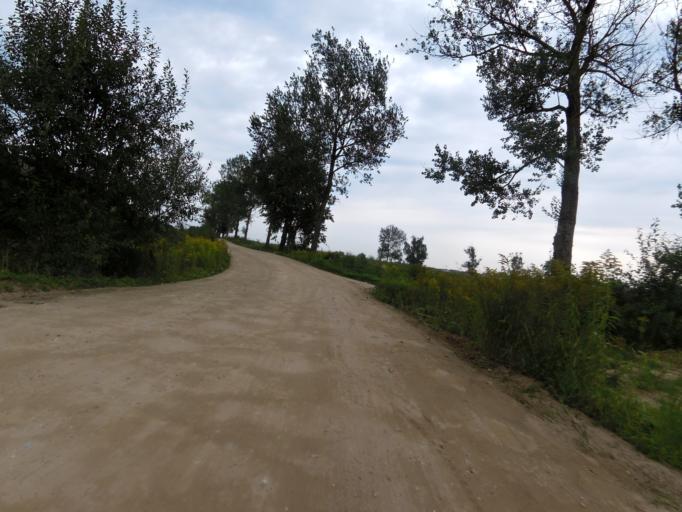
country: LT
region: Vilnius County
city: Pilaite
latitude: 54.7220
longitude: 25.1493
